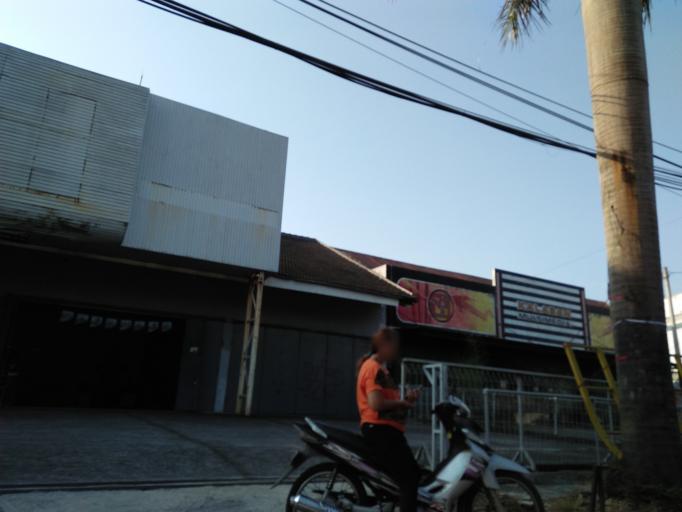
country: ID
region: Daerah Istimewa Yogyakarta
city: Depok
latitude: -7.7825
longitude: 110.4489
